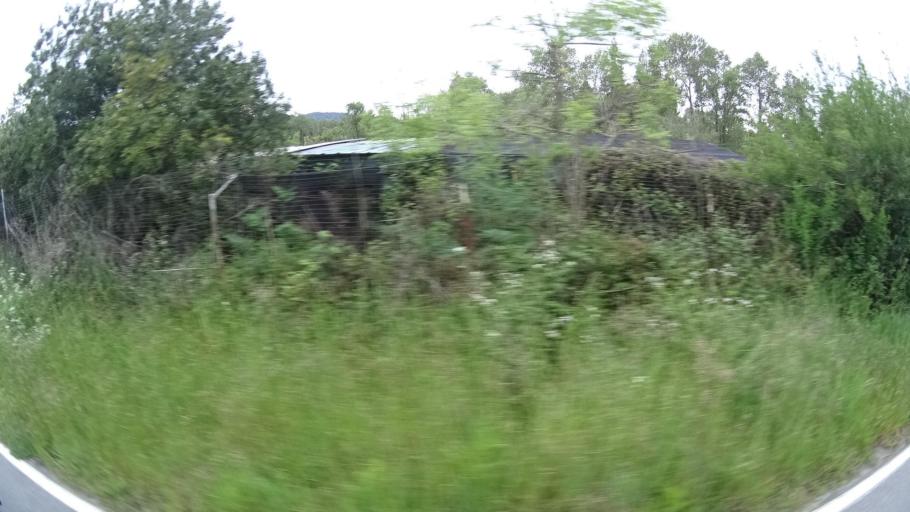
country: US
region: California
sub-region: Humboldt County
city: Blue Lake
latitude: 40.8715
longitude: -123.9939
